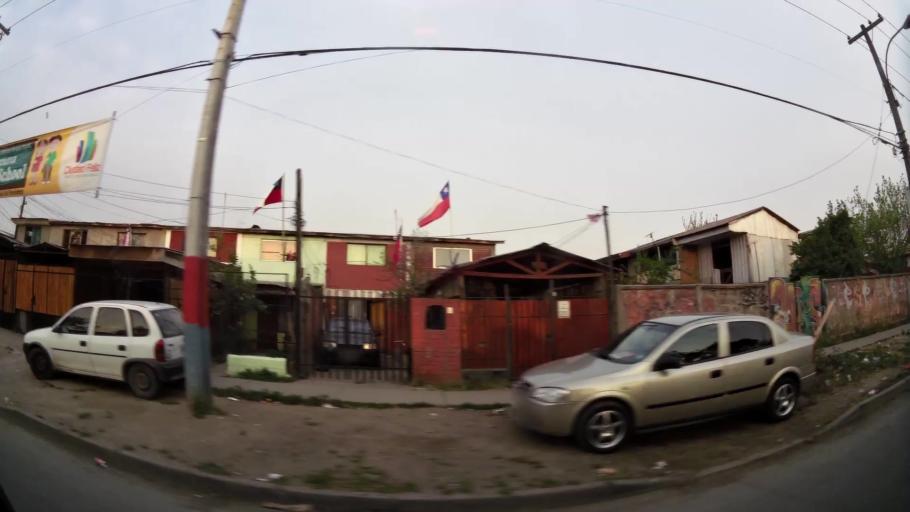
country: CL
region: Santiago Metropolitan
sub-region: Provincia de Santiago
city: Lo Prado
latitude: -33.5167
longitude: -70.7855
